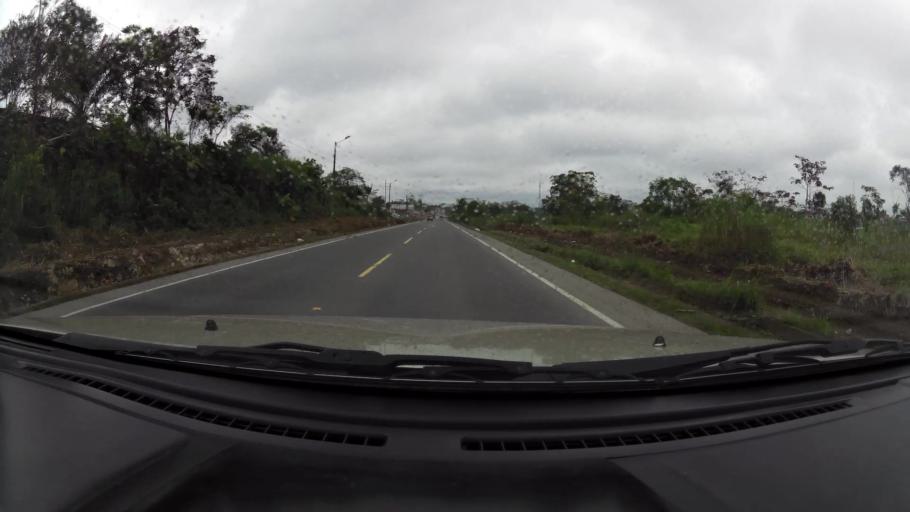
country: EC
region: Santo Domingo de los Tsachilas
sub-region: Canton Santo Domingo de los Colorados
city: Santo Domingo de los Colorados
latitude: -0.2742
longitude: -79.1627
